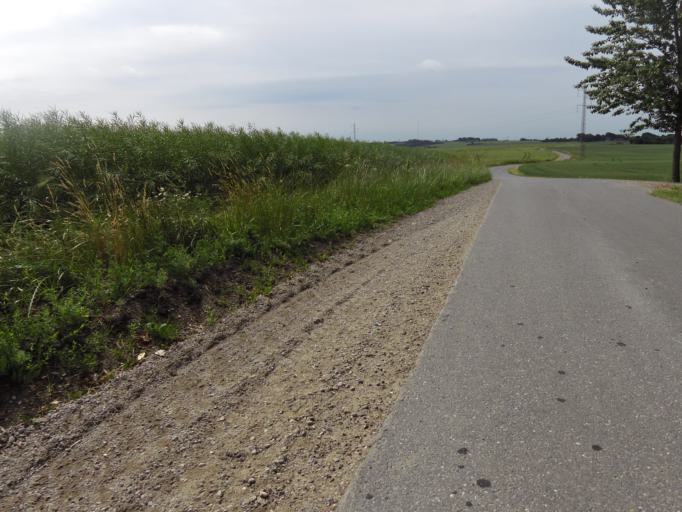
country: DK
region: Central Jutland
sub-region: Holstebro Kommune
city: Holstebro
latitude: 56.4280
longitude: 8.6677
